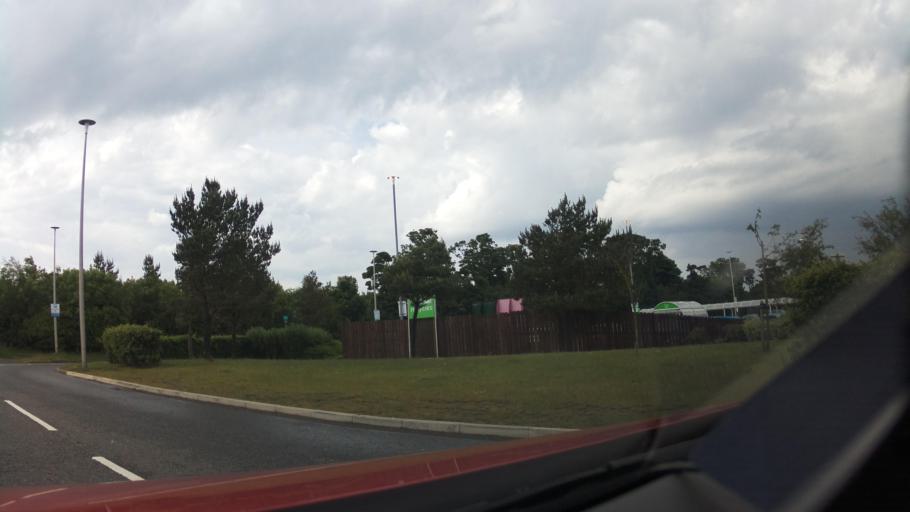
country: GB
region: Scotland
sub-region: East Lothian
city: Dunbar
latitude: 55.9890
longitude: -2.5117
